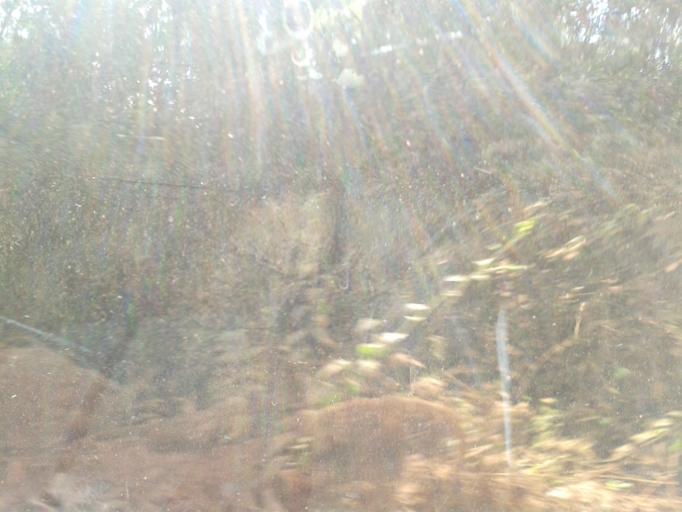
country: BR
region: Minas Gerais
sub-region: Ituiutaba
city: Ituiutaba
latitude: -19.0472
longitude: -49.3666
